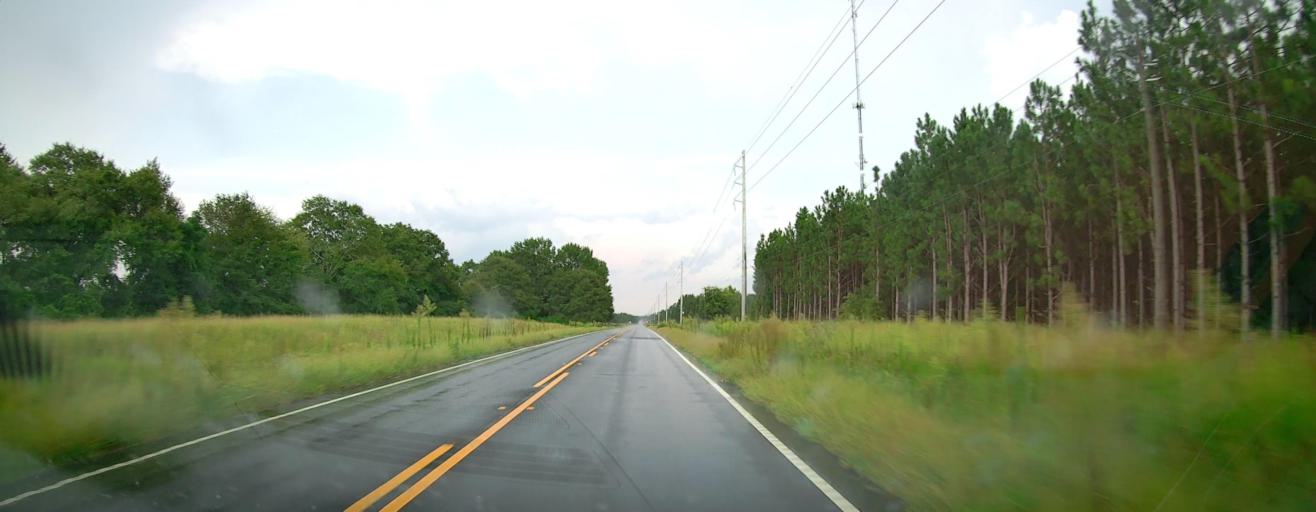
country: US
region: Georgia
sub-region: Dodge County
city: Chester
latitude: 32.5716
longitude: -83.1920
